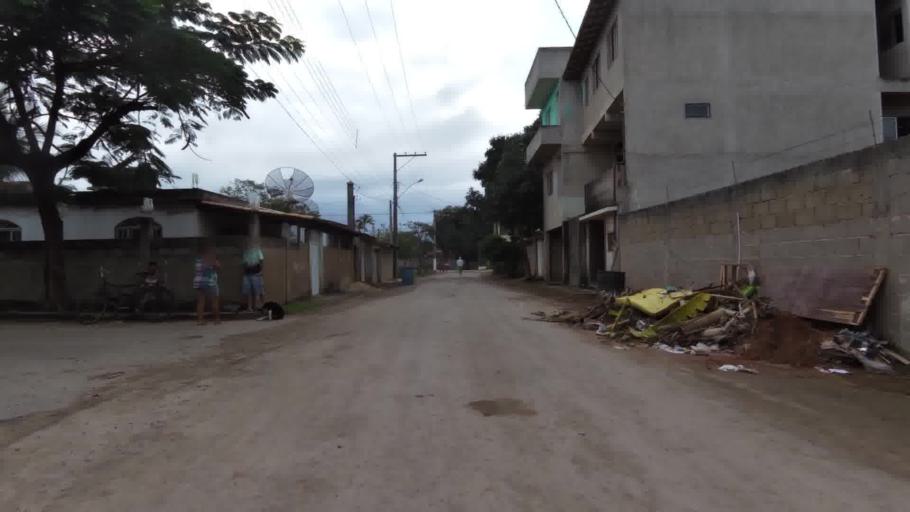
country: BR
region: Espirito Santo
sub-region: Piuma
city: Piuma
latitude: -20.8078
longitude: -40.6360
